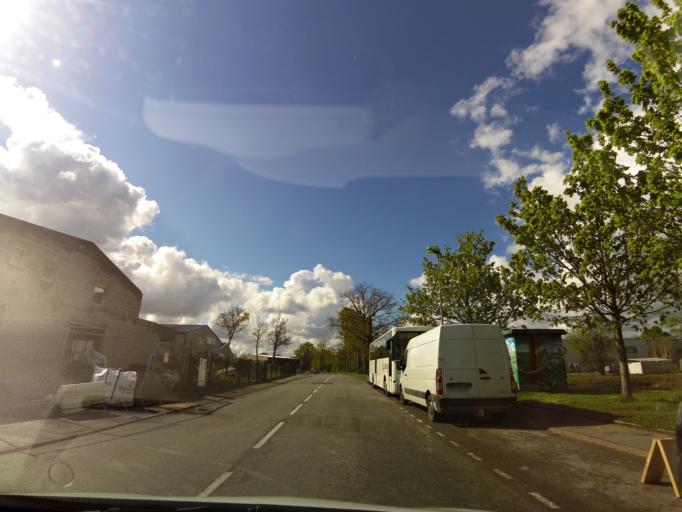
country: FR
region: Brittany
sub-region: Departement d'Ille-et-Vilaine
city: Saint-Erblon
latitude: 48.0173
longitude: -1.6600
